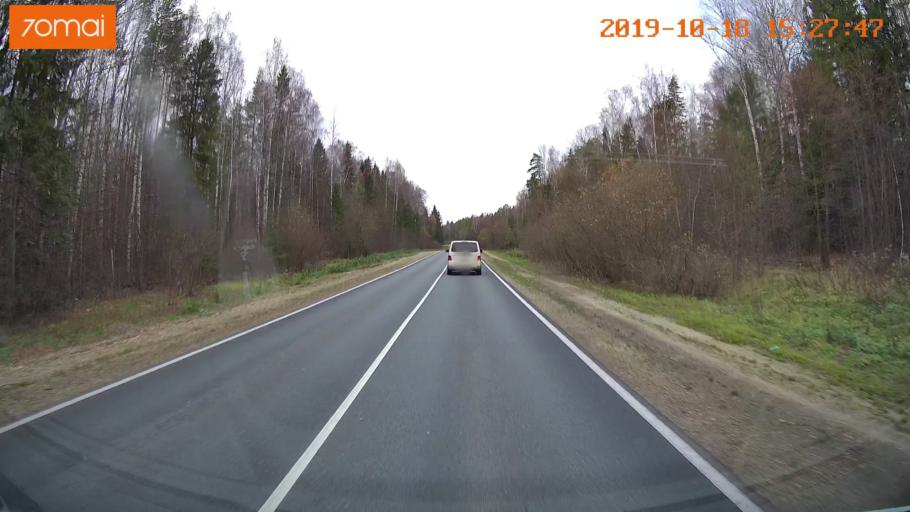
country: RU
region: Vladimir
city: Anopino
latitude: 55.7580
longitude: 40.6723
